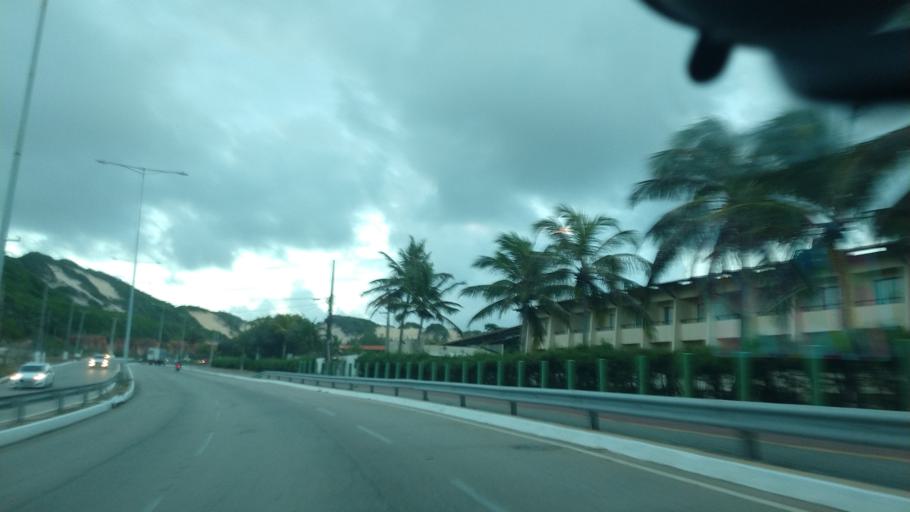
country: BR
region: Rio Grande do Norte
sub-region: Natal
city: Natal
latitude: -5.8097
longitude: -35.1819
